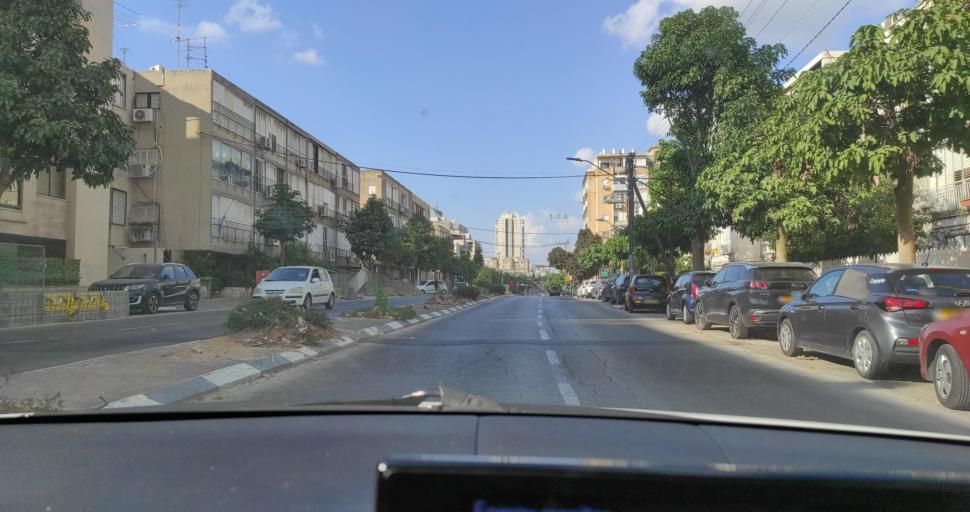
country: IL
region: Tel Aviv
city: Bene Beraq
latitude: 32.0643
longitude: 34.8284
